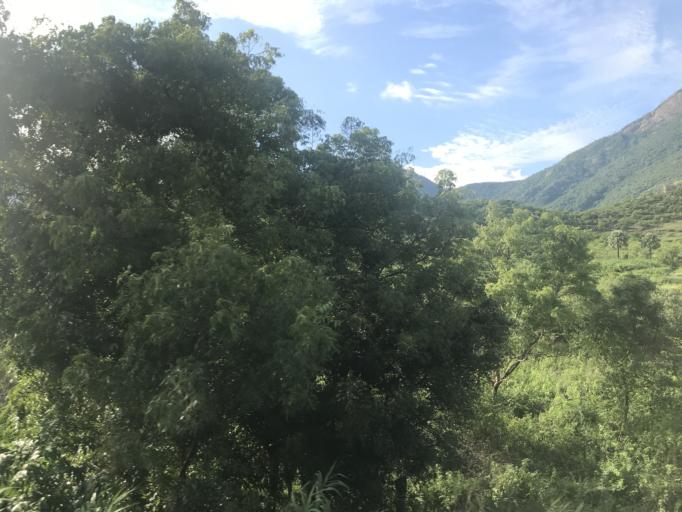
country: IN
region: Tamil Nadu
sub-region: Coimbatore
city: Madukkarai
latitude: 10.8923
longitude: 76.8820
